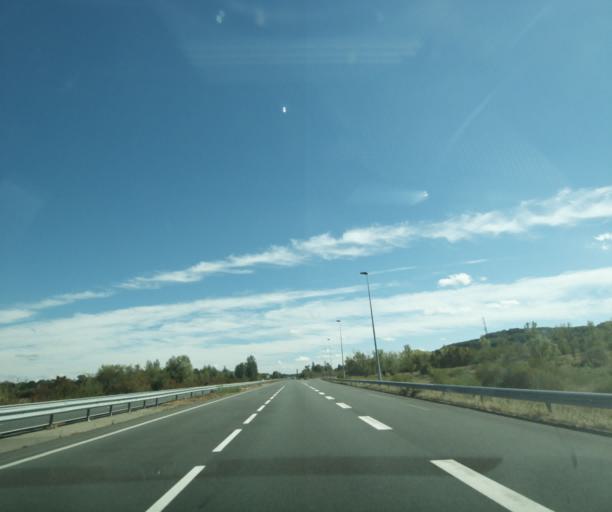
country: FR
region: Aquitaine
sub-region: Departement du Lot-et-Garonne
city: Sainte-Colombe-en-Bruilhois
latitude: 44.2008
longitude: 0.5005
